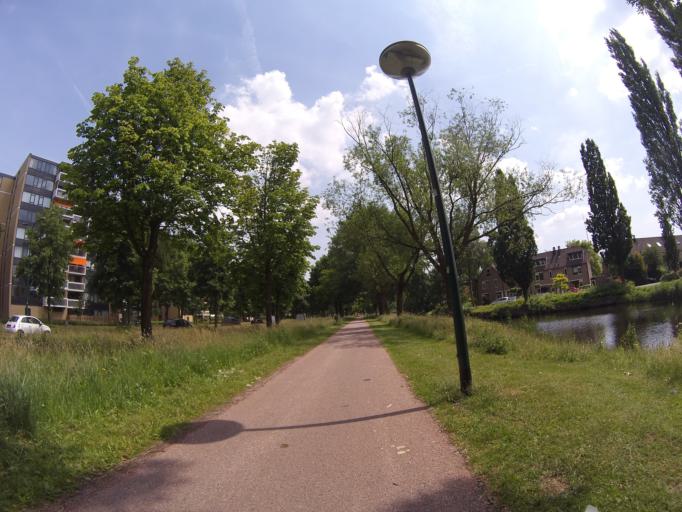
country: NL
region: Utrecht
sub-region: Gemeente Soest
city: Soest
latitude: 52.1730
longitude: 5.2799
